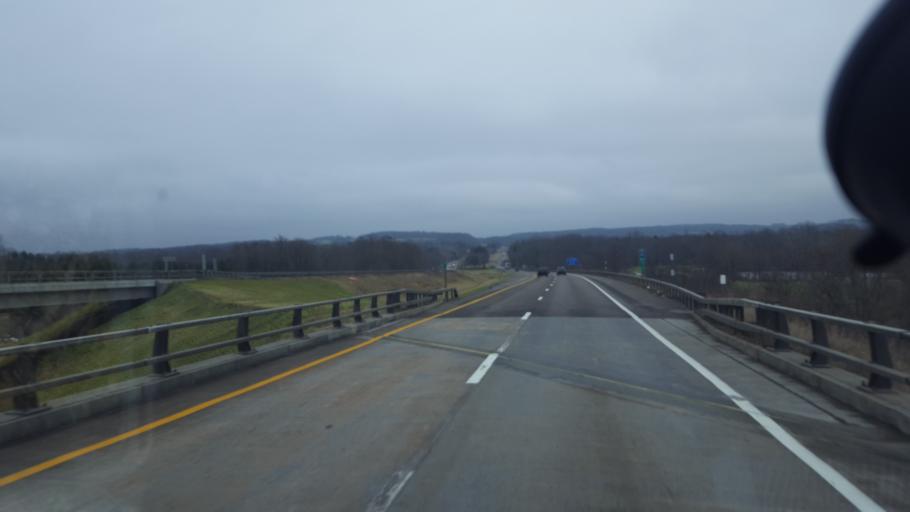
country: US
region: New York
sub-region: Chautauqua County
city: Falconer
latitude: 42.1397
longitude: -79.1098
